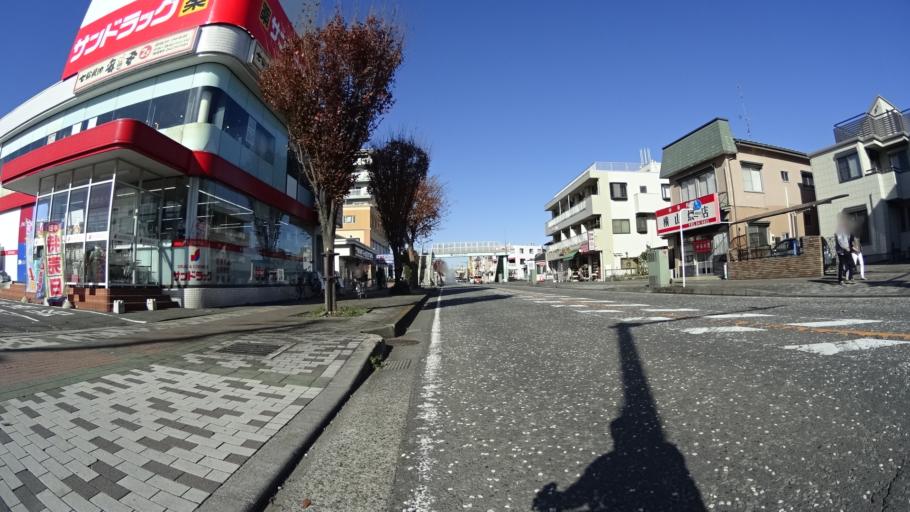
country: JP
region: Kanagawa
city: Zama
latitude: 35.5657
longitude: 139.3608
